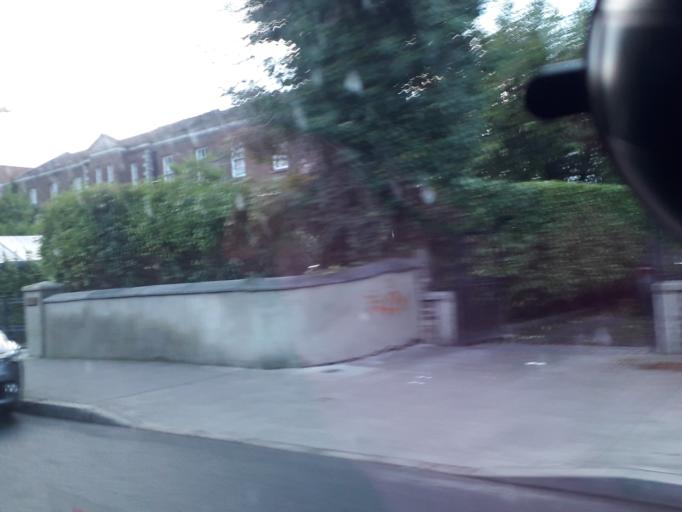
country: IE
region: Leinster
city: Rathgar
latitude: 53.3152
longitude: -6.2719
